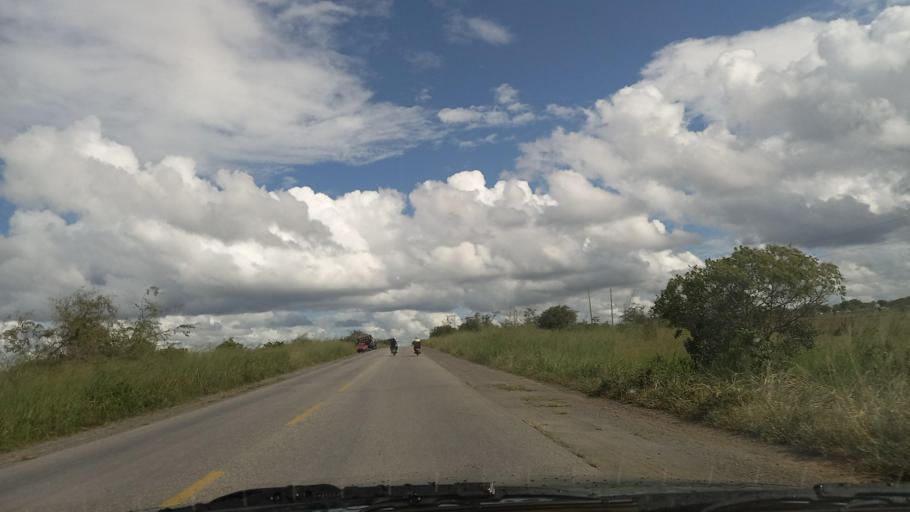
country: BR
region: Pernambuco
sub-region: Lajedo
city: Lajedo
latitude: -8.5929
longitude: -36.2906
